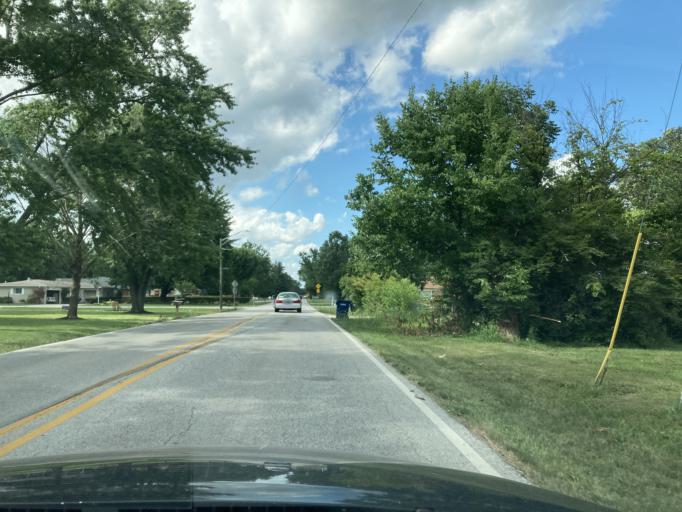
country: US
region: Indiana
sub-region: Marion County
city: Meridian Hills
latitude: 39.8643
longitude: -86.2121
